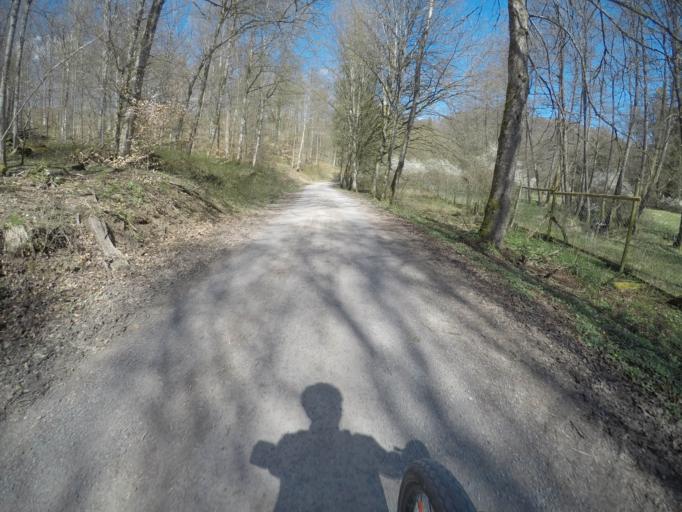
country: DE
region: Baden-Wuerttemberg
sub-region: Regierungsbezirk Stuttgart
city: Hildrizhausen
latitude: 48.5902
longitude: 8.9748
